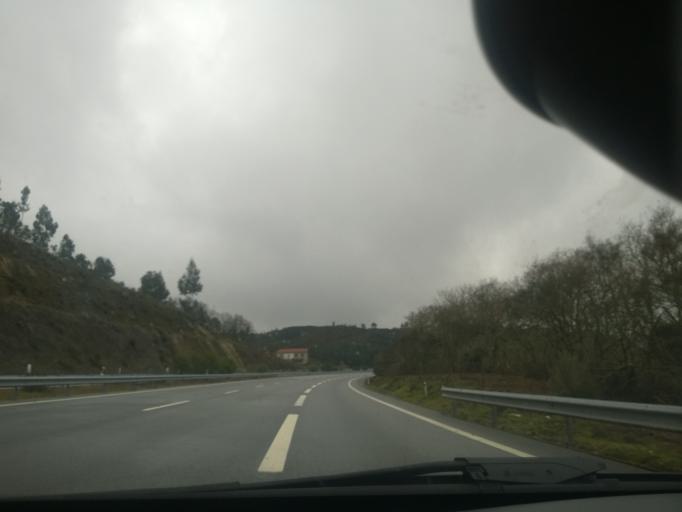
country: PT
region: Braga
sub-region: Celorico de Basto
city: Celorico de Basto
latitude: 41.4482
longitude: -8.0535
